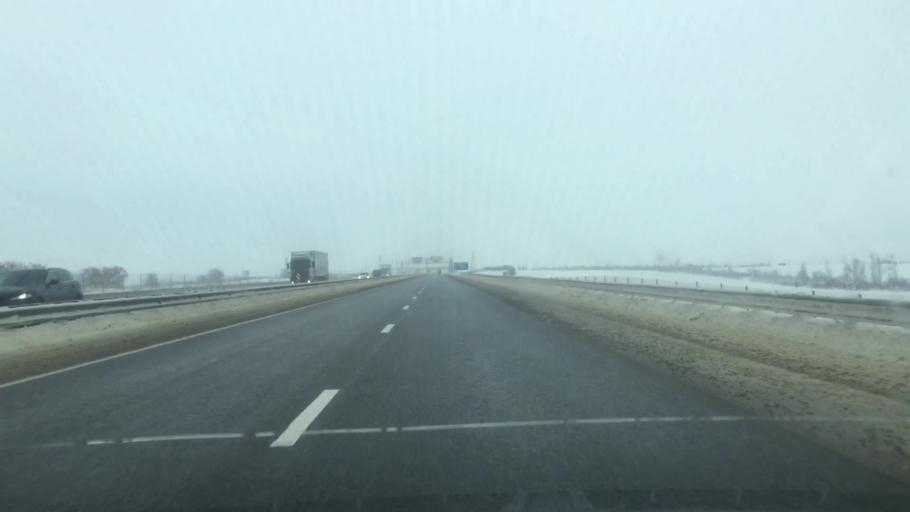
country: RU
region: Tula
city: Yefremov
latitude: 53.2178
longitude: 38.2144
